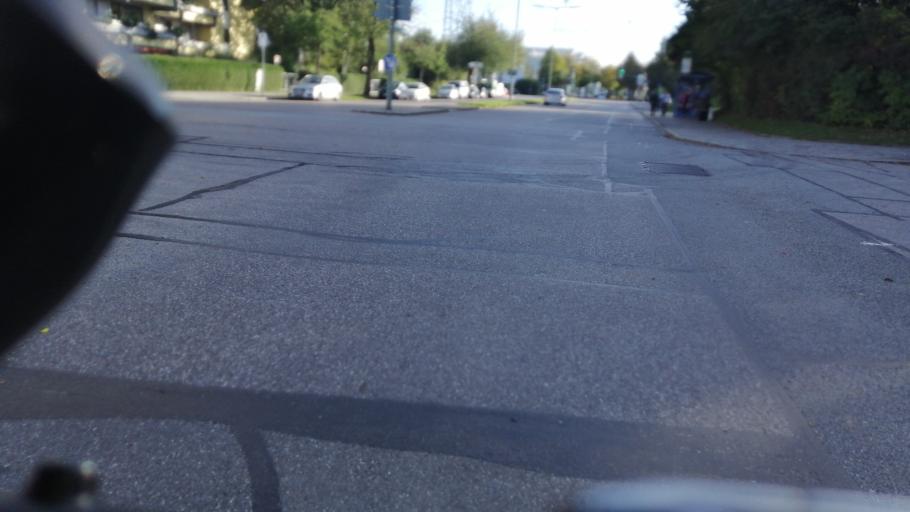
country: DE
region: Bavaria
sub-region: Upper Bavaria
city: Unterfoehring
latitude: 48.2011
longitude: 11.6118
